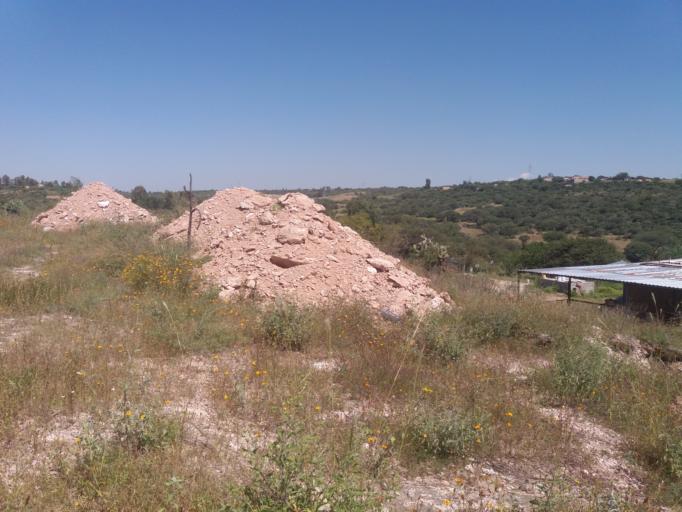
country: MX
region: Aguascalientes
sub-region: Aguascalientes
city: San Sebastian [Fraccionamiento]
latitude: 21.7750
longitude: -102.2339
